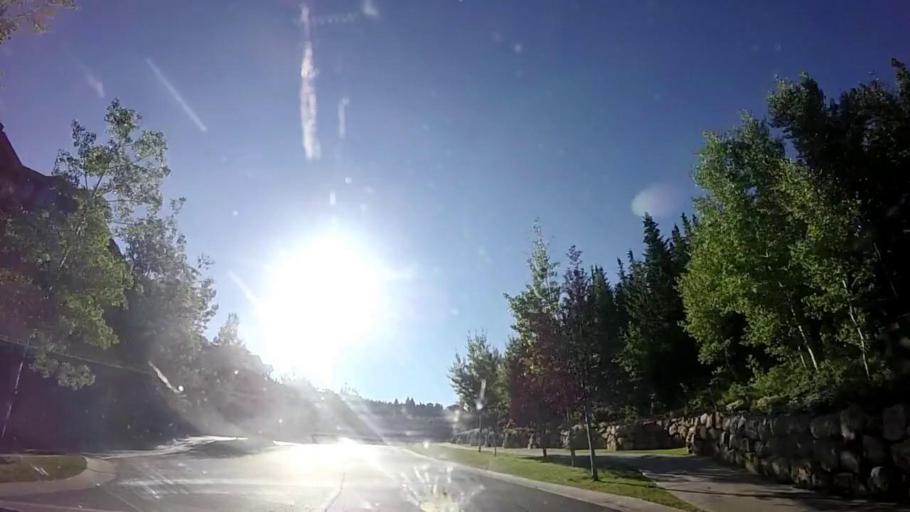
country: US
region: Utah
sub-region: Summit County
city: Park City
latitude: 40.6234
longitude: -111.4912
